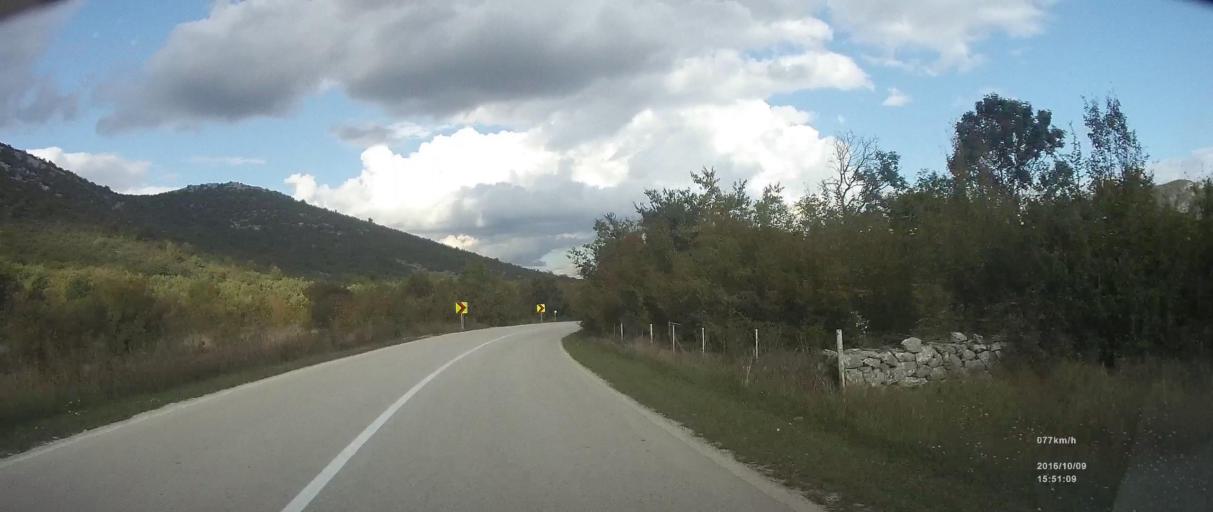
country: HR
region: Splitsko-Dalmatinska
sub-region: Grad Trogir
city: Trogir
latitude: 43.6041
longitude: 16.2065
